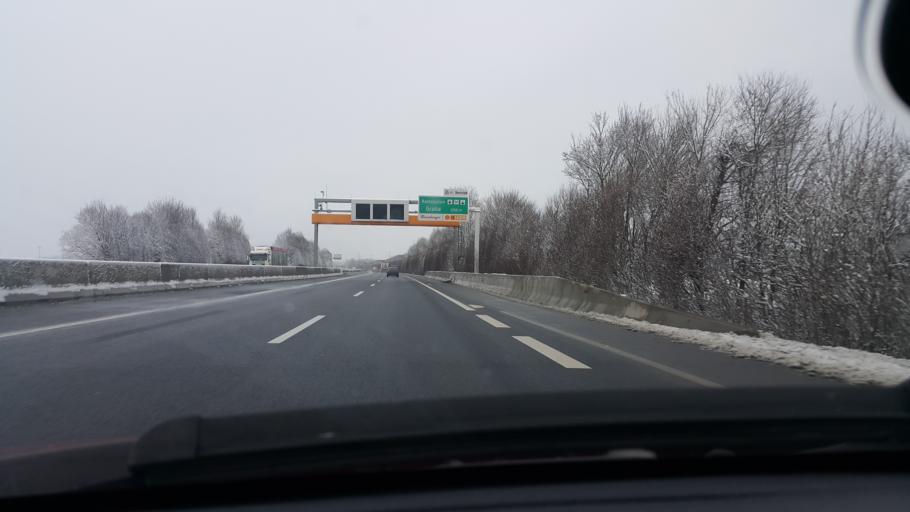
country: AT
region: Styria
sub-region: Politischer Bezirk Leibnitz
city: Kaindorf an der Sulm
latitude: 46.8118
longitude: 15.5669
